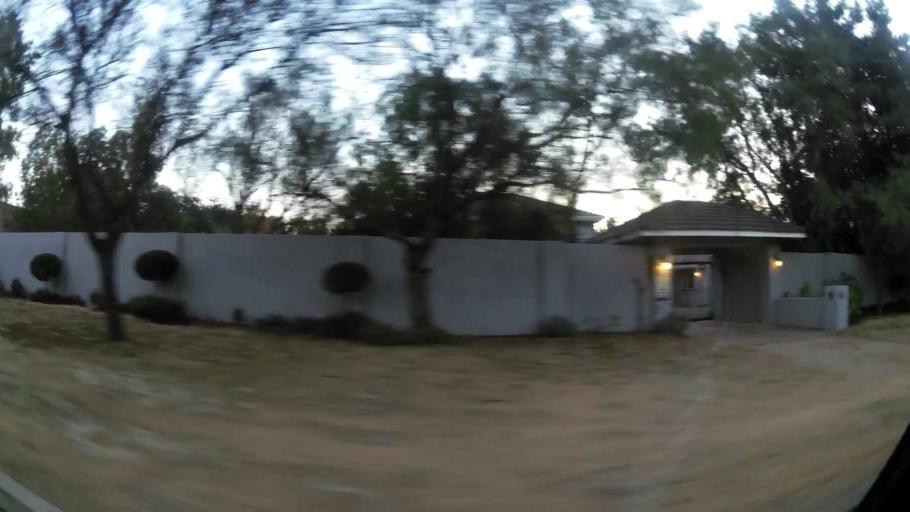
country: ZA
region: Gauteng
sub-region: City of Johannesburg Metropolitan Municipality
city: Midrand
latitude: -25.9830
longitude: 28.0650
